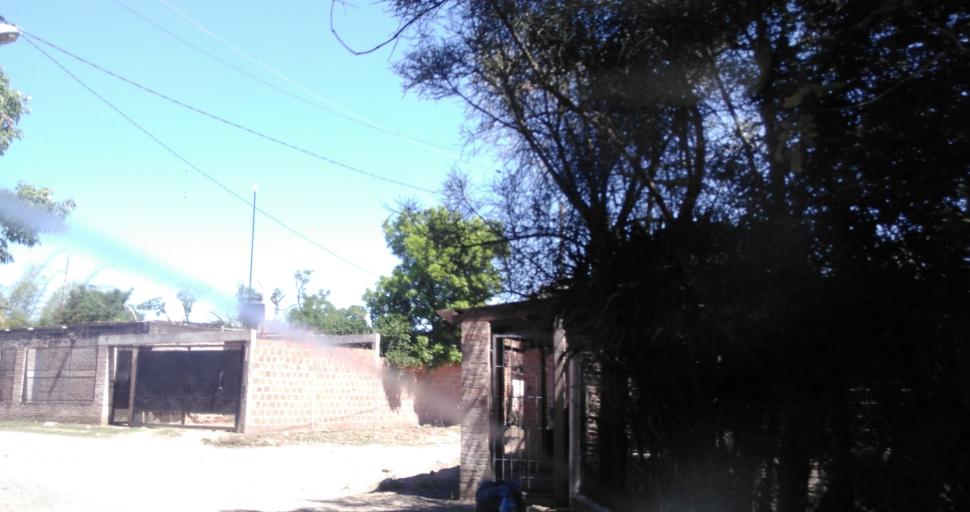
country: AR
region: Chaco
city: Resistencia
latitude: -27.4236
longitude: -58.9835
